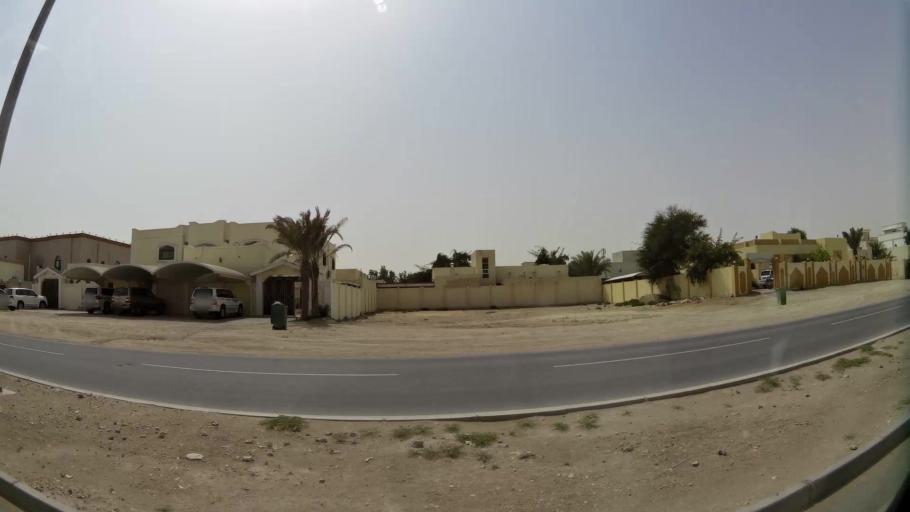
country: QA
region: Baladiyat ar Rayyan
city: Ar Rayyan
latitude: 25.2460
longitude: 51.3781
